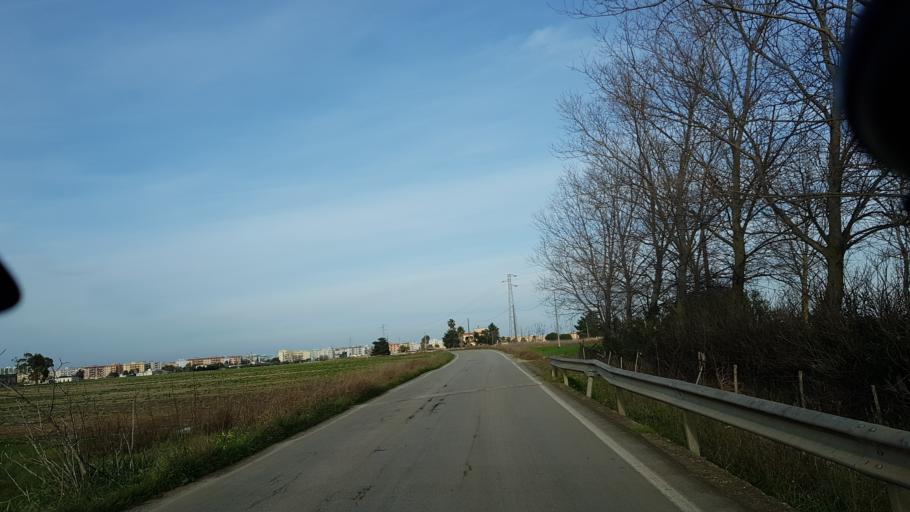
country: IT
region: Apulia
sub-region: Provincia di Brindisi
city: Brindisi
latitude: 40.6080
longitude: 17.9116
